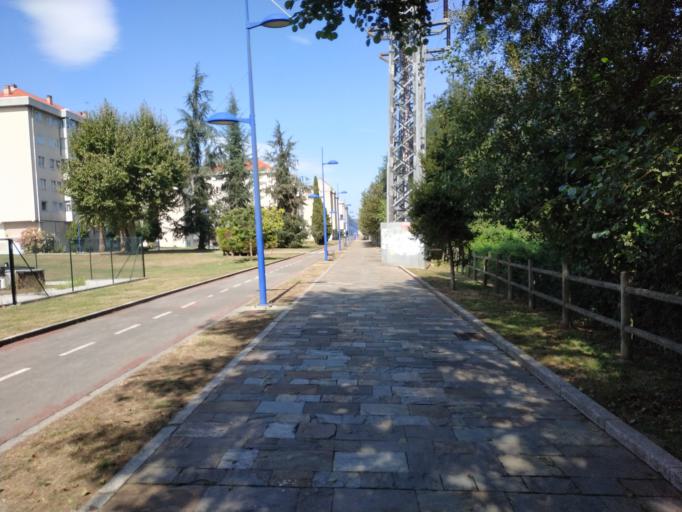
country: ES
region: Galicia
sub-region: Provincia da Coruna
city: Culleredo
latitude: 43.3143
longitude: -8.3727
